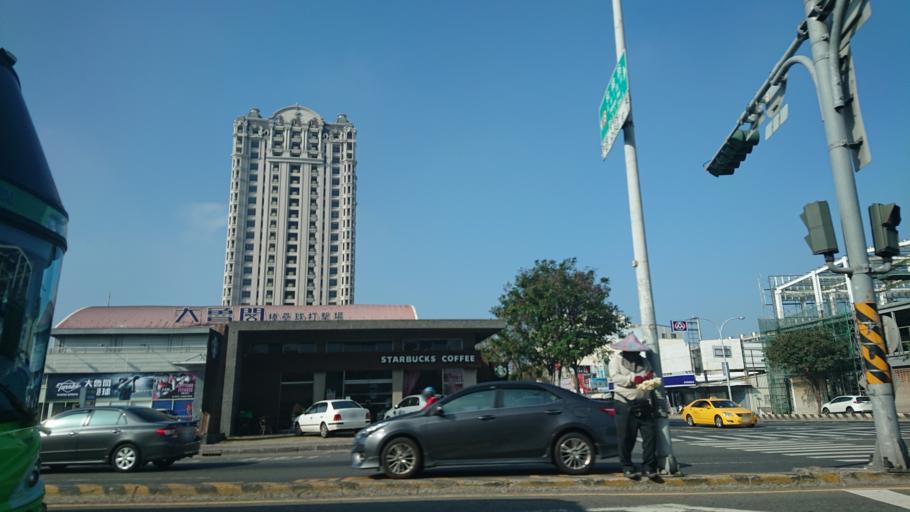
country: TW
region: Taiwan
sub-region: Tainan
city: Tainan
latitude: 23.0066
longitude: 120.1864
